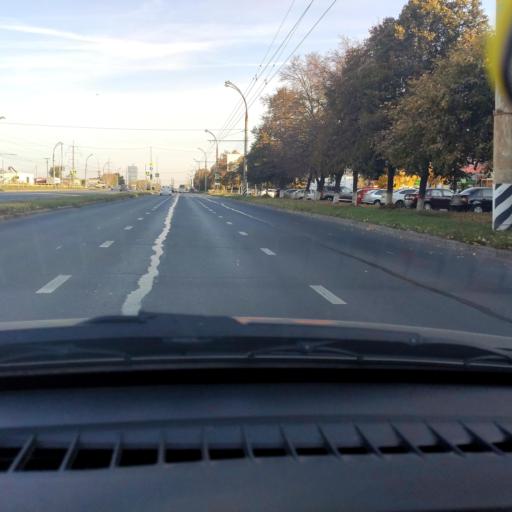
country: RU
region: Samara
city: Tol'yatti
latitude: 53.5356
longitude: 49.2629
